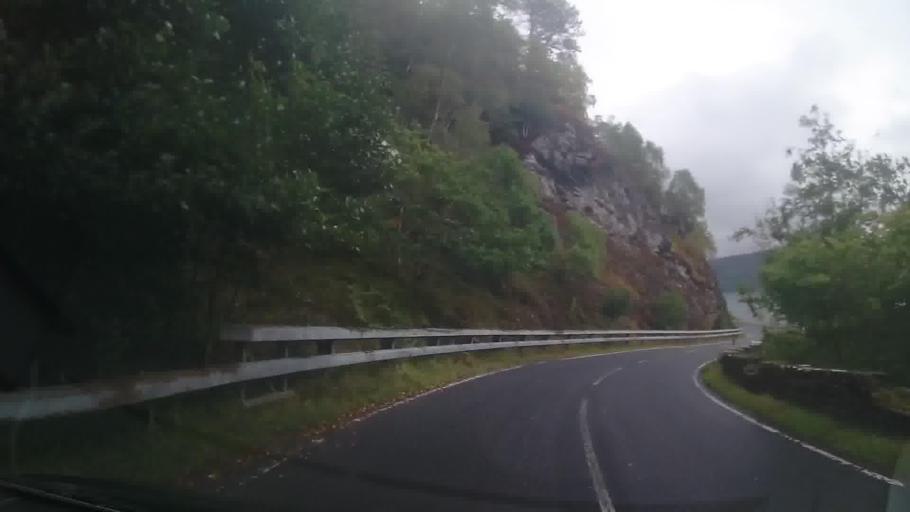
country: GB
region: Scotland
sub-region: Argyll and Bute
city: Isle Of Mull
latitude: 56.6775
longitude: -5.8765
